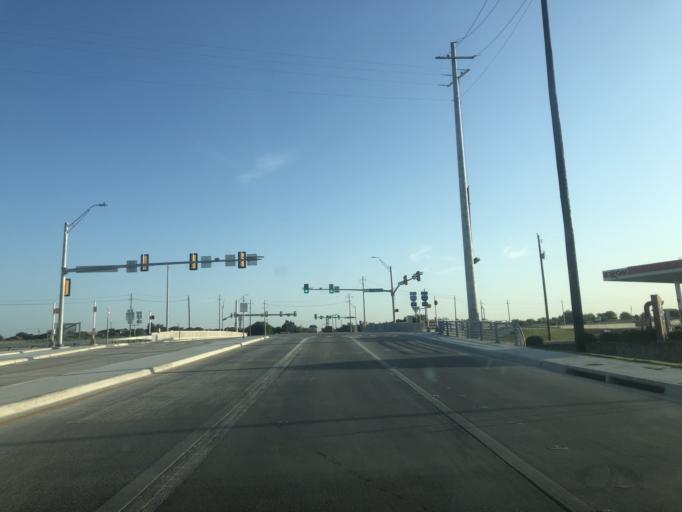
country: US
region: Texas
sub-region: Tarrant County
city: White Settlement
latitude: 32.7284
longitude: -97.5037
